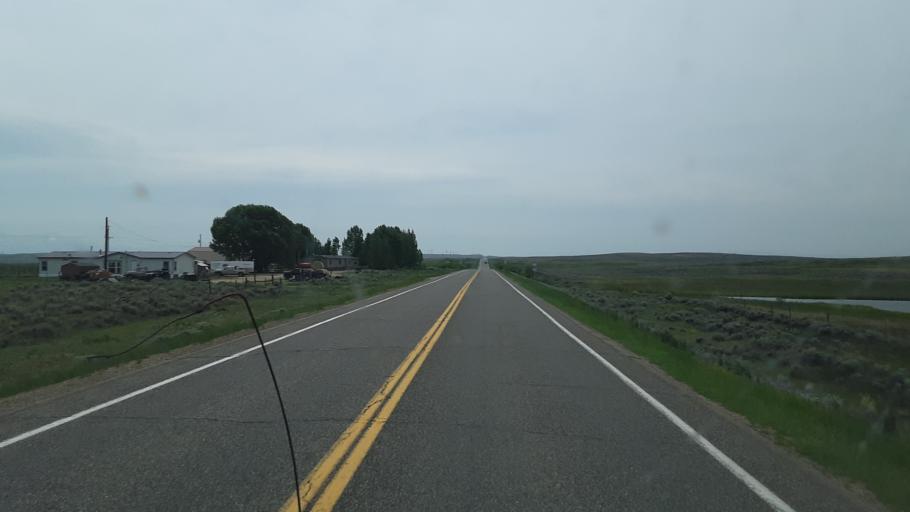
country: US
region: Colorado
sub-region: Jackson County
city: Walden
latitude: 40.8563
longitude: -106.3116
